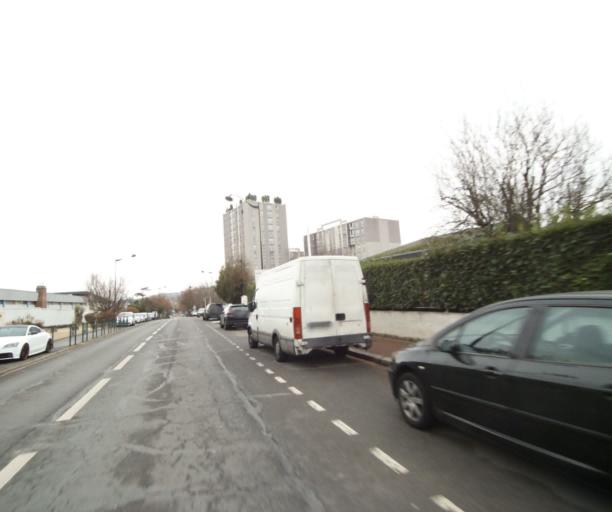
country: FR
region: Ile-de-France
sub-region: Departement des Hauts-de-Seine
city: Rueil-Malmaison
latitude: 48.8667
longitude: 2.1769
